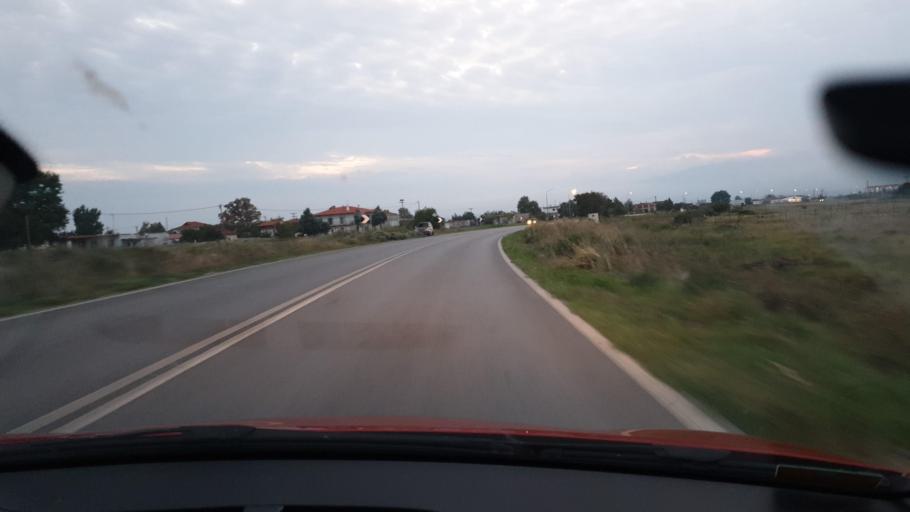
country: GR
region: Central Macedonia
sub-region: Nomos Kilkis
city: Polykastro
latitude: 40.9910
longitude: 22.6192
